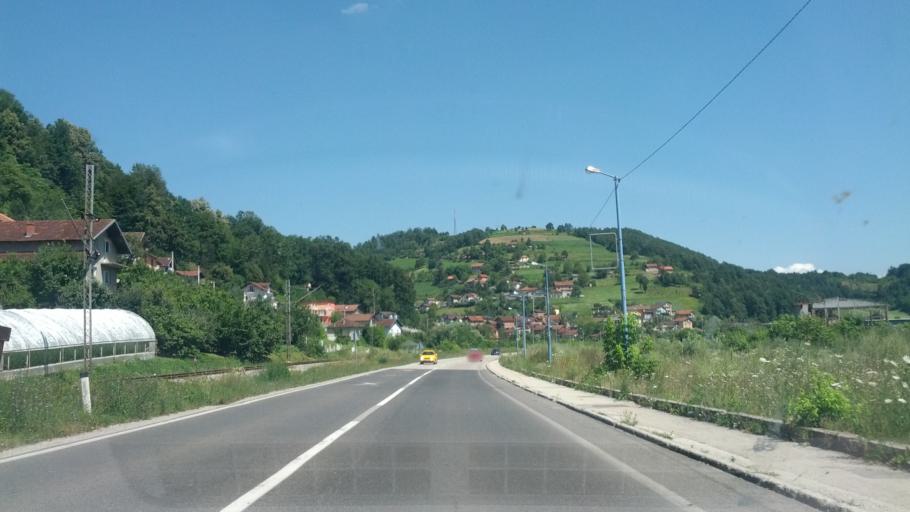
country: BA
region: Federation of Bosnia and Herzegovina
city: Bosanska Krupa
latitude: 44.8911
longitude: 16.1541
